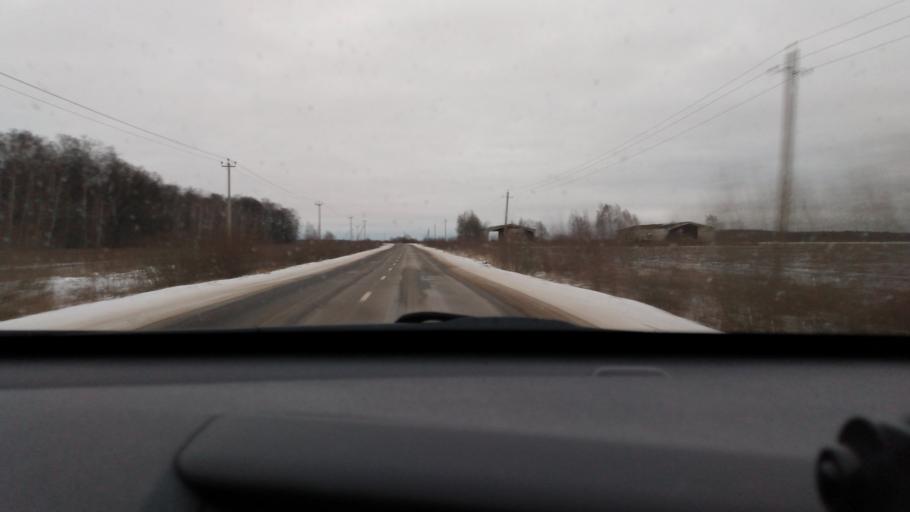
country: RU
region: Moskovskaya
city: Meshcherino
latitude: 55.2899
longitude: 38.3050
